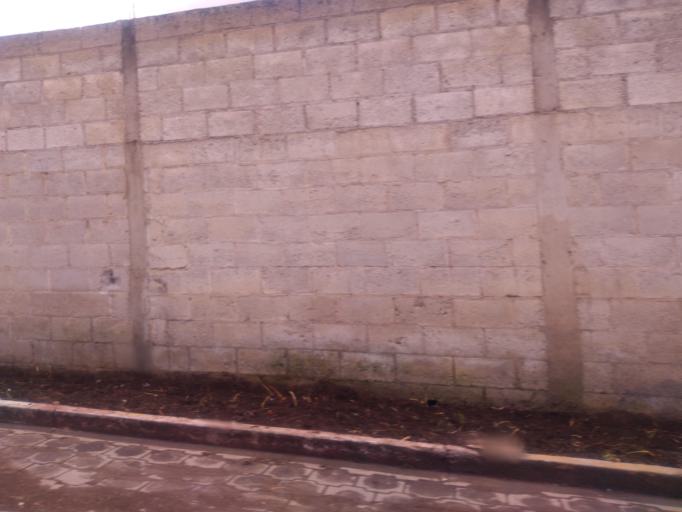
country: GT
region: Quetzaltenango
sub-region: Municipio de La Esperanza
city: La Esperanza
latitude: 14.8707
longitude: -91.5628
